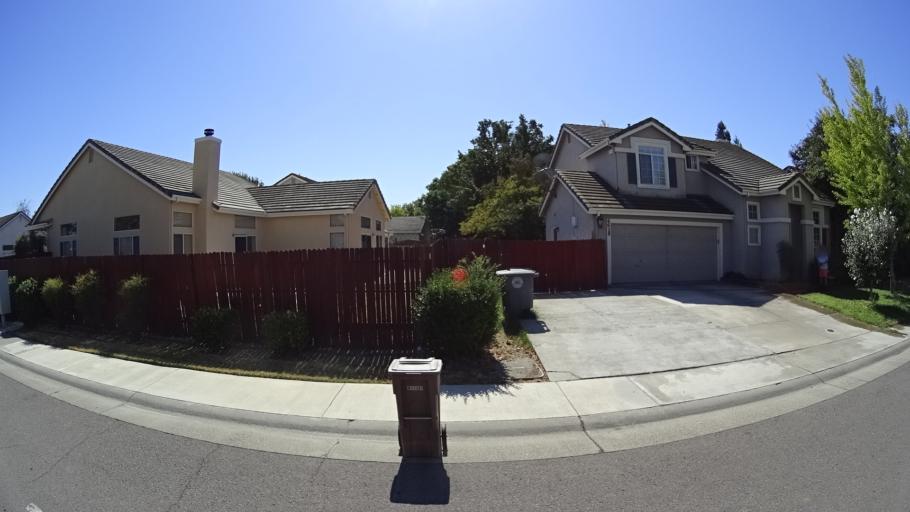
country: US
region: California
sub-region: Sacramento County
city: Laguna
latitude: 38.4282
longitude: -121.4247
